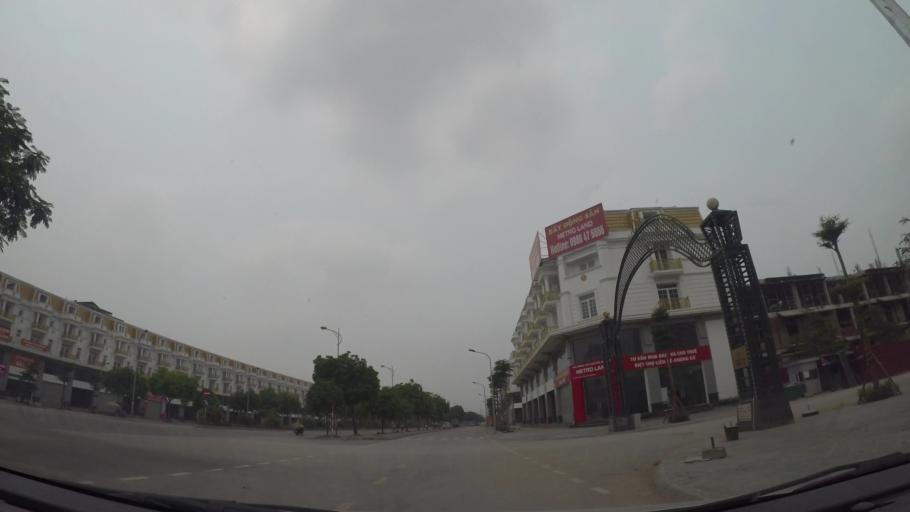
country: VN
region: Ha Noi
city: Ha Dong
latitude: 20.9838
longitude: 105.7409
